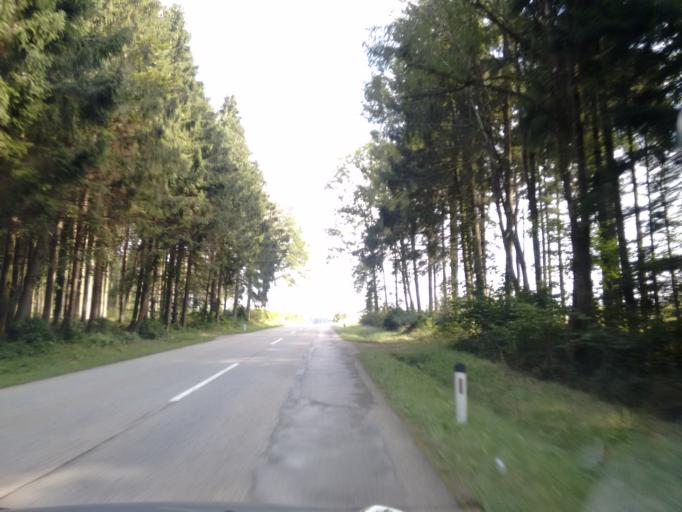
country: AT
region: Upper Austria
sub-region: Wels-Land
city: Thalheim bei Wels
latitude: 48.1282
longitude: 14.0826
